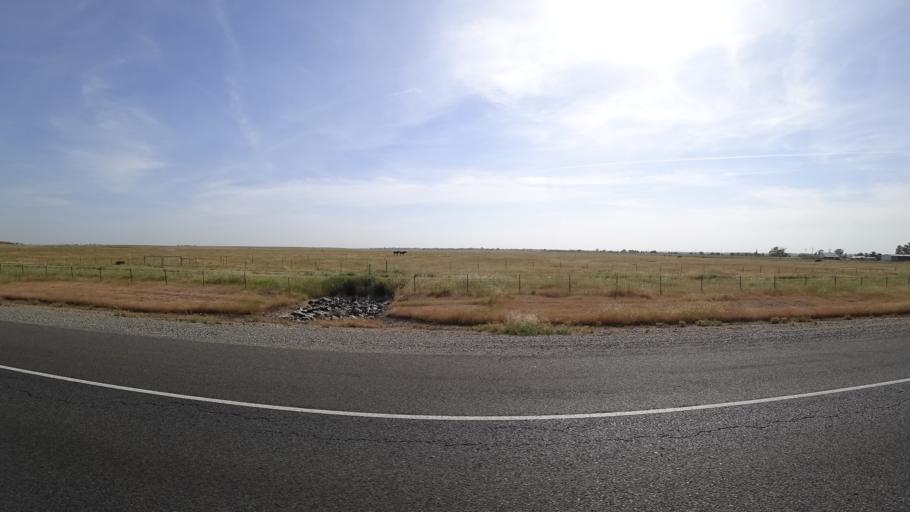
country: US
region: California
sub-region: Butte County
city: Durham
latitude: 39.6281
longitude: -121.7002
